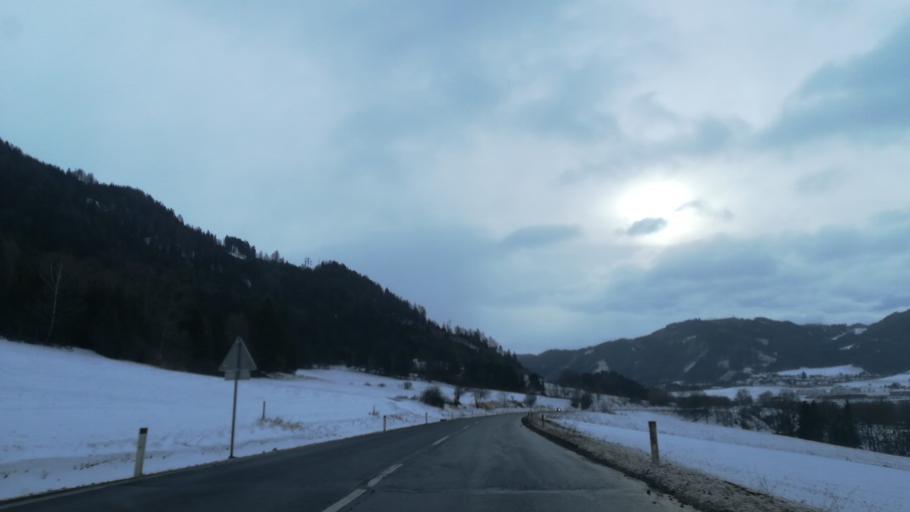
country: AT
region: Styria
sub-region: Politischer Bezirk Murtal
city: Sankt Peter ob Judenburg
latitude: 47.1972
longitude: 14.5945
